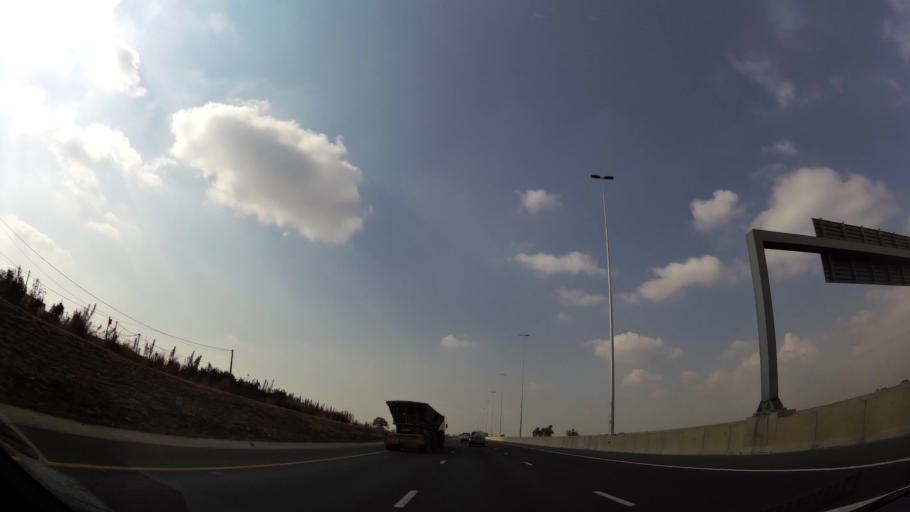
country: ZA
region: Gauteng
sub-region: Ekurhuleni Metropolitan Municipality
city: Benoni
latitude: -26.1669
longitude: 28.3782
